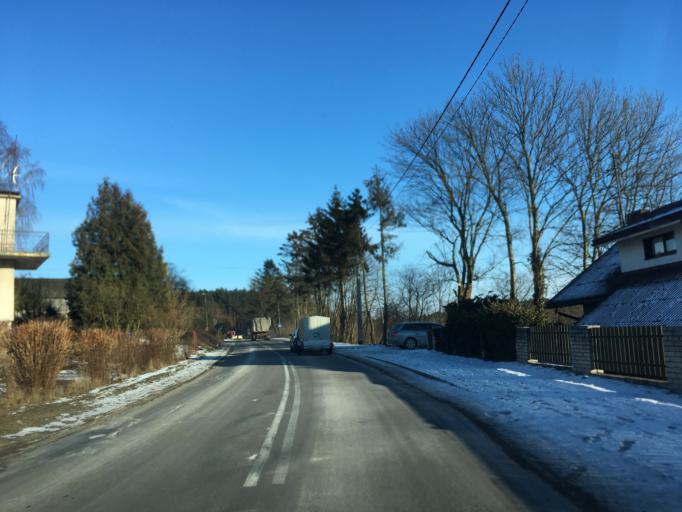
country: PL
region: Pomeranian Voivodeship
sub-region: Powiat starogardzki
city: Zblewo
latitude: 53.8849
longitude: 18.3512
